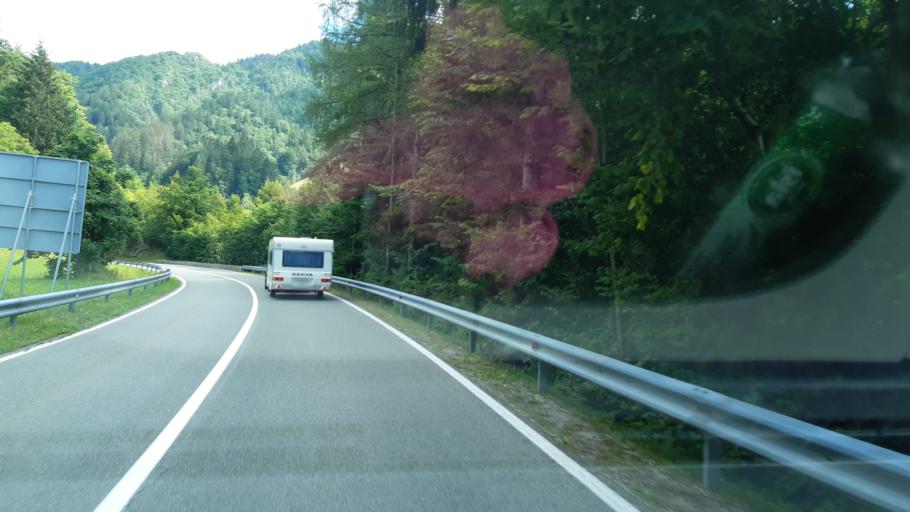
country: SI
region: Trzic
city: Trzic
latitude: 46.3668
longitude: 14.3066
